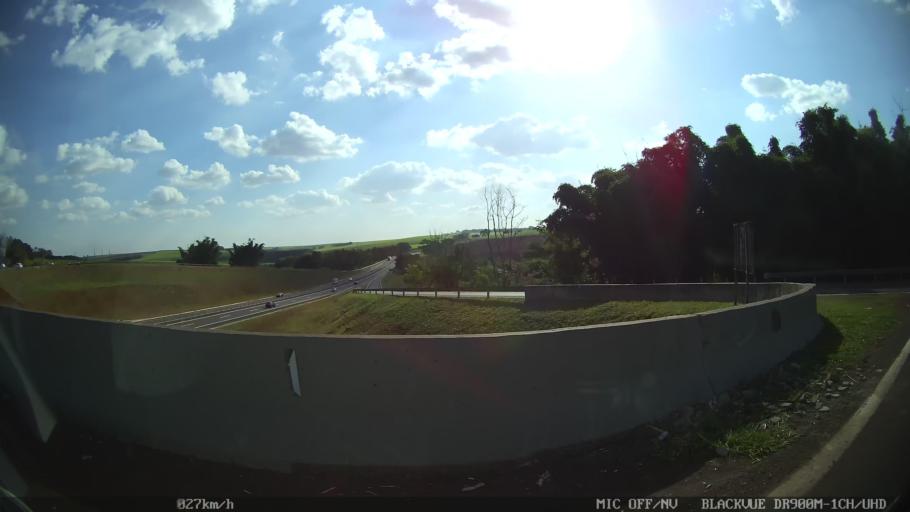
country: BR
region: Sao Paulo
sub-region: Ribeirao Preto
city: Ribeirao Preto
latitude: -21.1975
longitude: -47.8767
